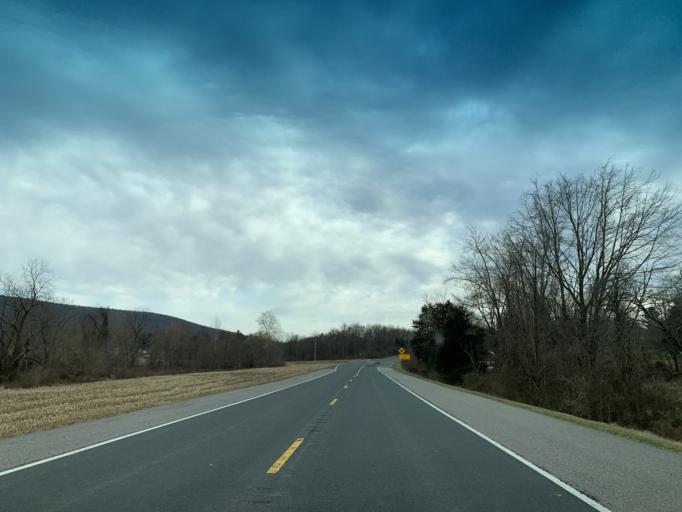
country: US
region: Maryland
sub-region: Washington County
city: Keedysville
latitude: 39.4349
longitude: -77.6613
